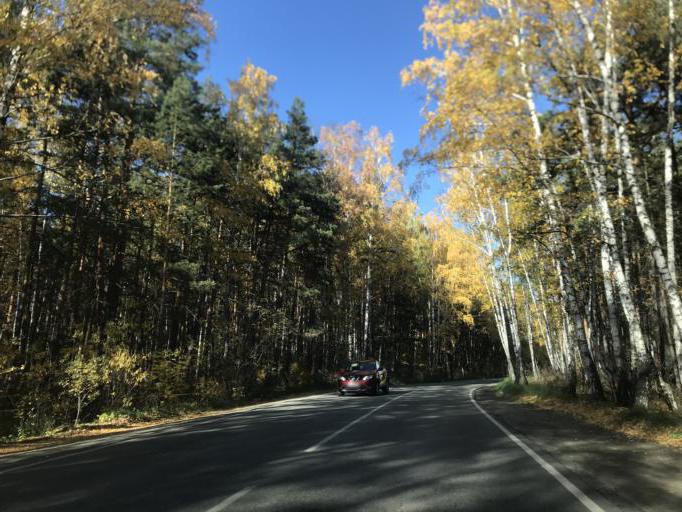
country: RU
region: Chelyabinsk
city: Dolgoderevenskoye
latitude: 55.2908
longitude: 61.3561
